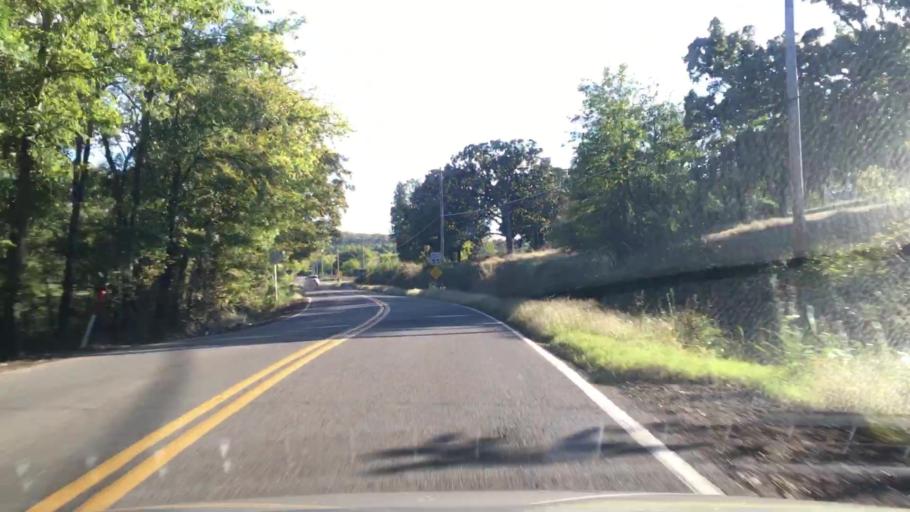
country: US
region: Oklahoma
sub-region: Muskogee County
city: Fort Gibson
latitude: 35.9241
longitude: -95.1541
